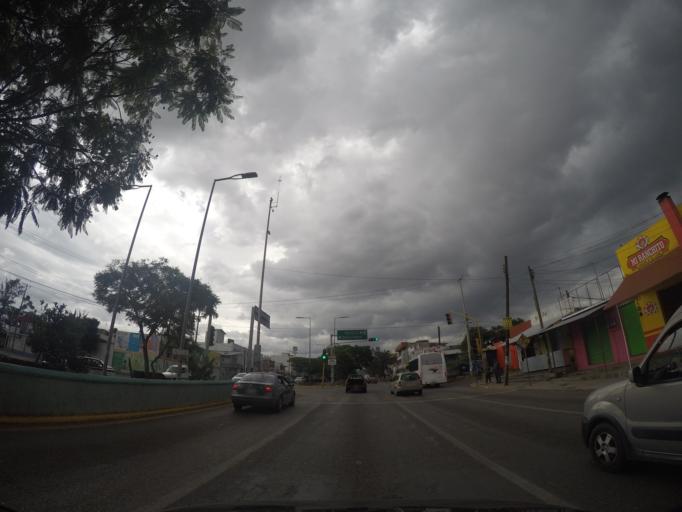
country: MX
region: Oaxaca
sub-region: Santa Cruz Amilpas
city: Santa Cruz Amilpas
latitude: 17.0695
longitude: -96.7019
